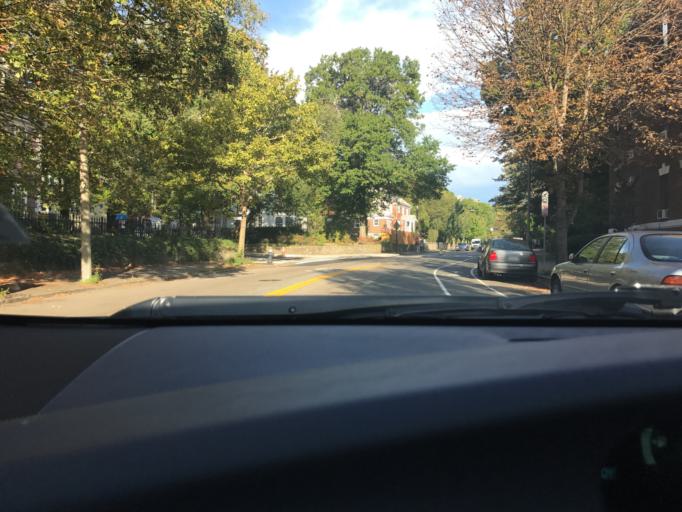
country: US
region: Massachusetts
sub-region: Norfolk County
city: Brookline
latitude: 42.3351
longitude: -71.1245
